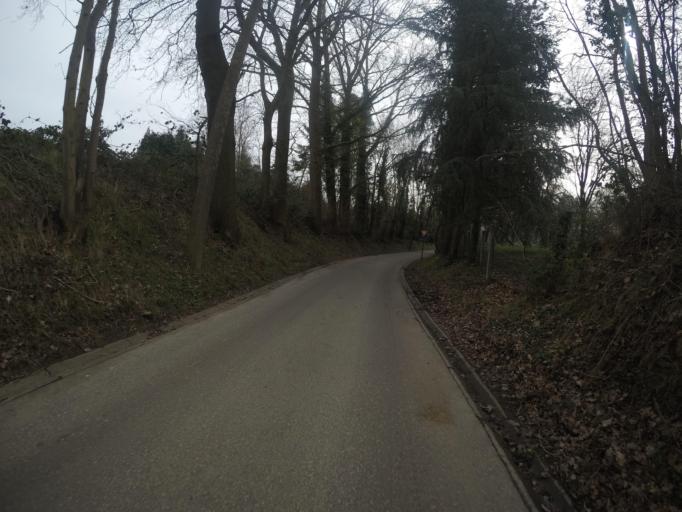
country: BE
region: Flanders
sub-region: Provincie Oost-Vlaanderen
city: Sint-Maria-Lierde
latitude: 50.8140
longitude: 3.8083
